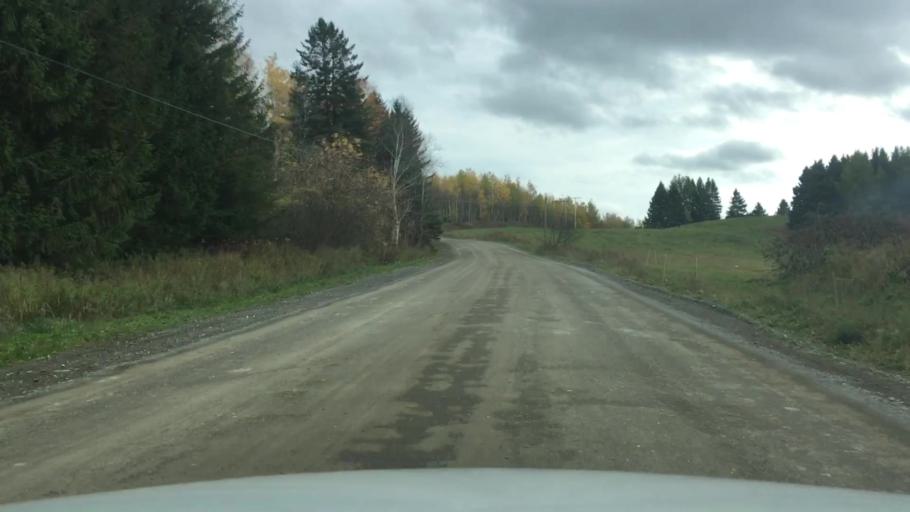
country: US
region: Maine
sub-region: Aroostook County
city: Easton
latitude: 46.5190
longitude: -67.8863
